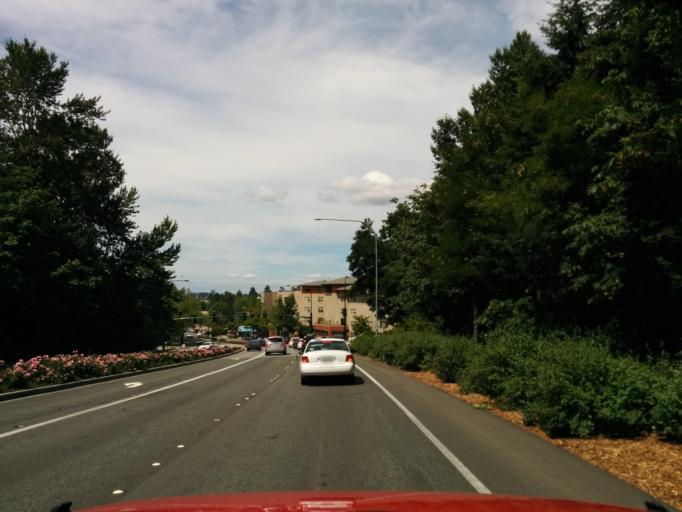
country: US
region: Washington
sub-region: King County
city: Kirkland
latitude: 47.6795
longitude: -122.1954
